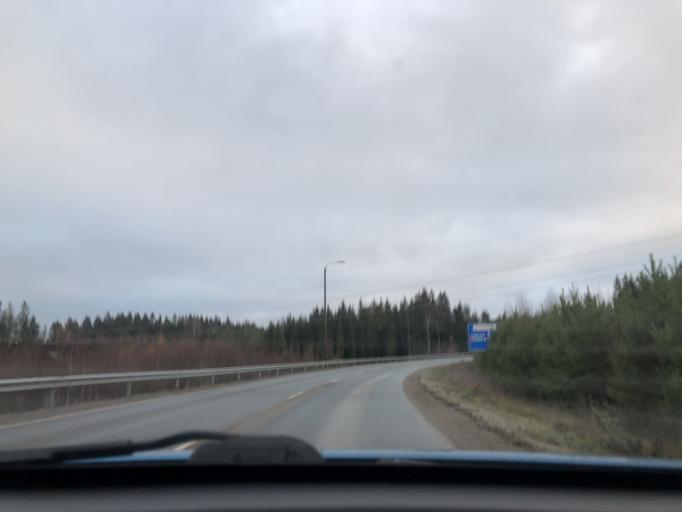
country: FI
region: Pirkanmaa
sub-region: Tampere
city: Kangasala
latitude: 61.5347
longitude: 23.9847
